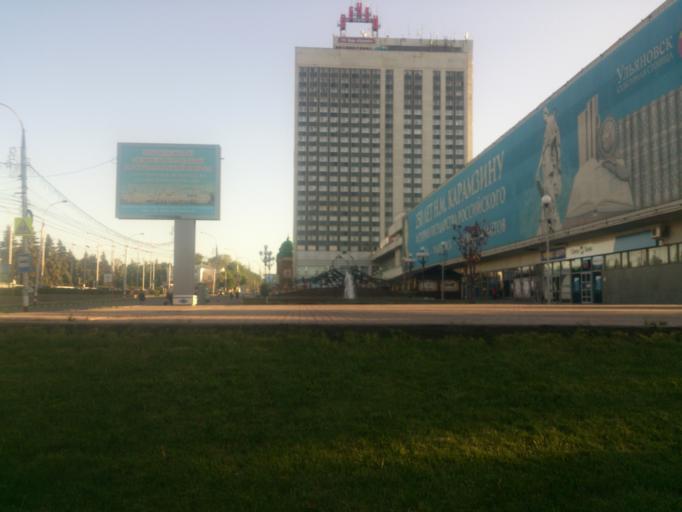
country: RU
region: Ulyanovsk
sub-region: Ulyanovskiy Rayon
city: Ulyanovsk
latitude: 54.3209
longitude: 48.4046
